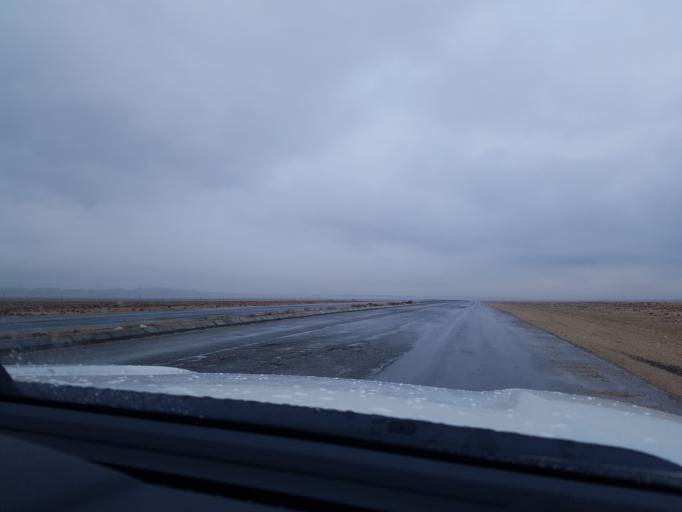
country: TM
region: Balkan
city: Turkmenbasy
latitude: 40.0644
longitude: 53.3640
